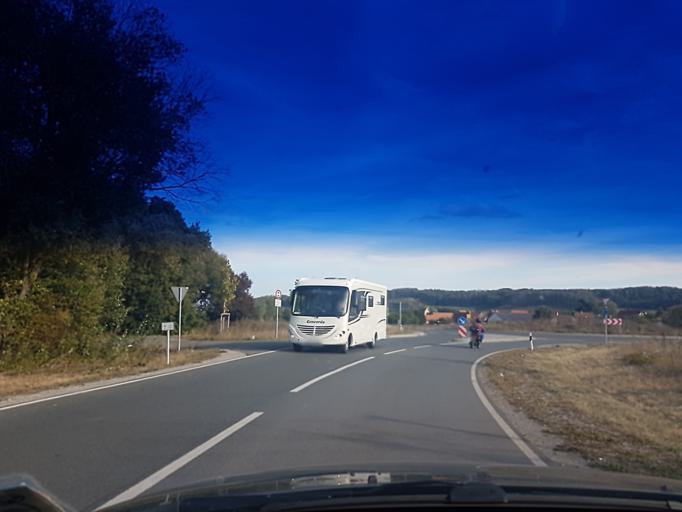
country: DE
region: Bavaria
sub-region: Regierungsbezirk Mittelfranken
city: Burghaslach
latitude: 49.7672
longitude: 10.5673
